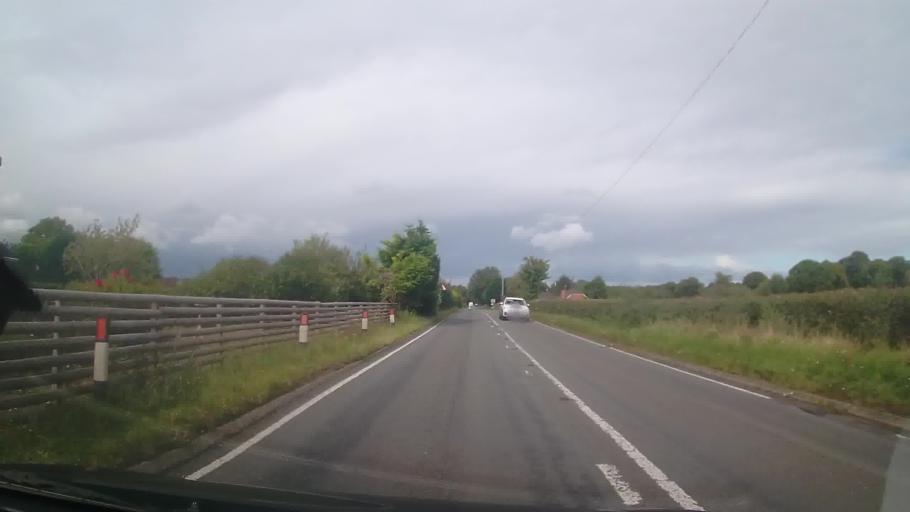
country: GB
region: England
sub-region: Shropshire
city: Alveley
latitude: 52.4474
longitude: -2.3377
